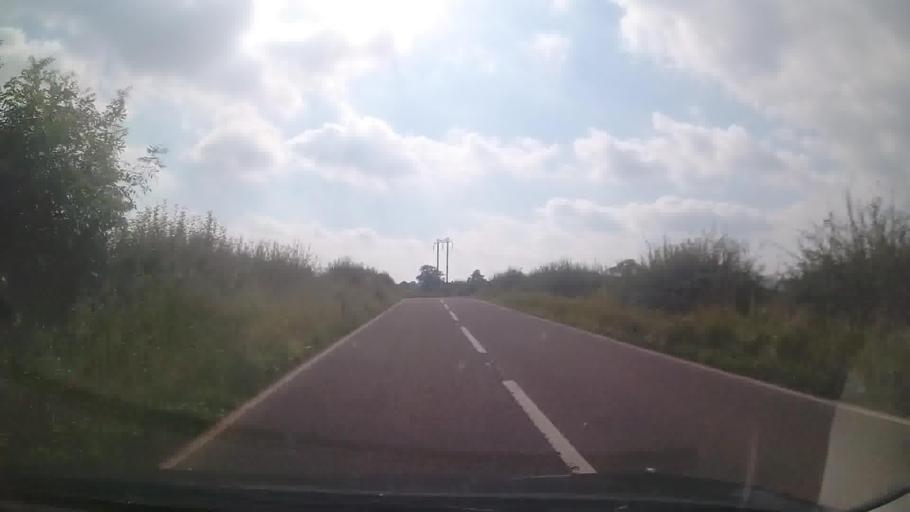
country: GB
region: England
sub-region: Cheshire West and Chester
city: Bickley
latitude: 53.0226
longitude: -2.6872
